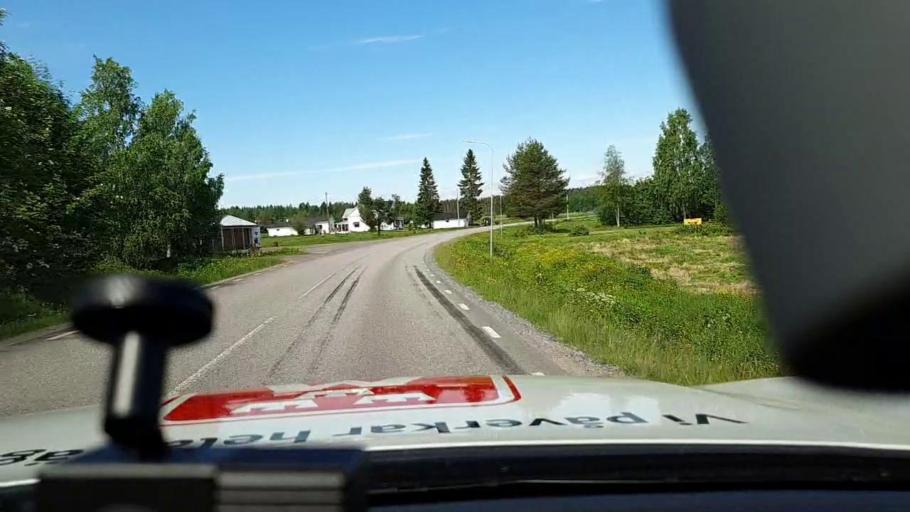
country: SE
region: Norrbotten
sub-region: Lulea Kommun
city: Sodra Sunderbyn
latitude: 65.6603
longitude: 21.8307
